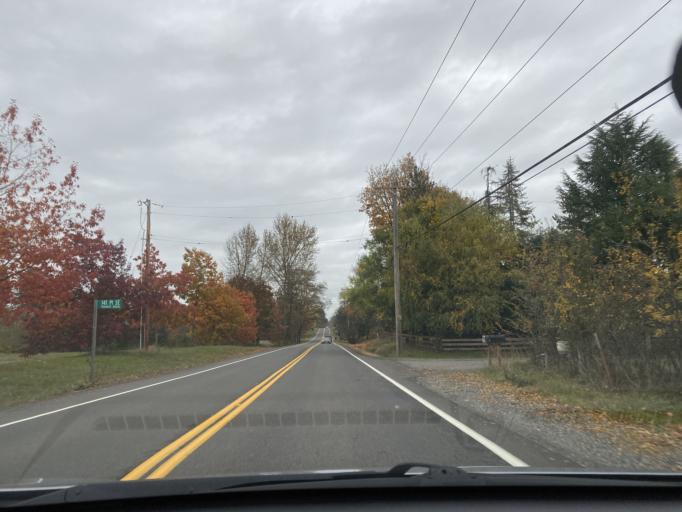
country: US
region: Washington
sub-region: King County
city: Lea Hill
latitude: 47.3007
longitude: -122.1533
